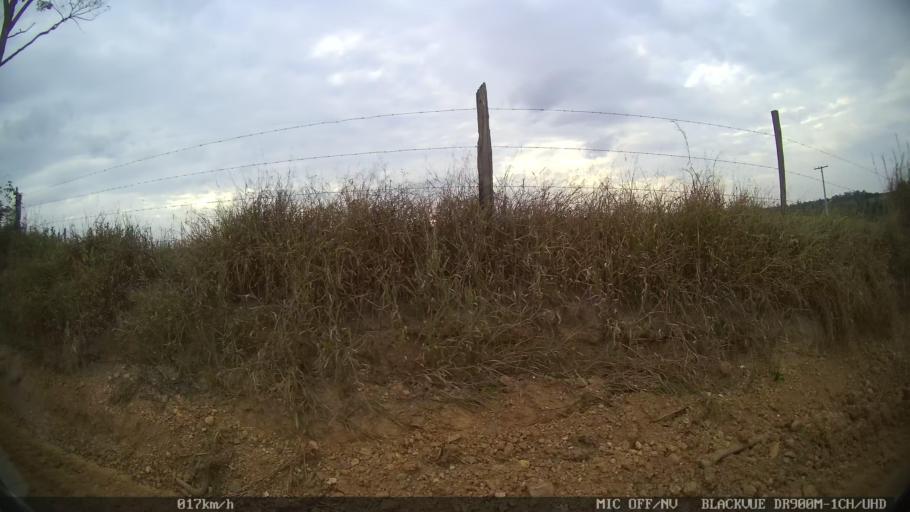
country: BR
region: Sao Paulo
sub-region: Americana
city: Americana
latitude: -22.6797
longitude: -47.3803
